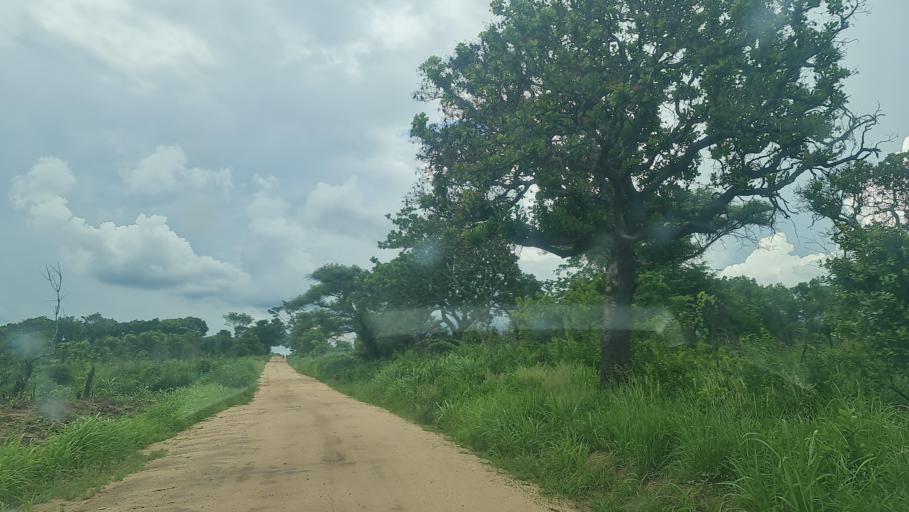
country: MW
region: Southern Region
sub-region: Nsanje District
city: Nsanje
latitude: -17.5818
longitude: 35.6643
